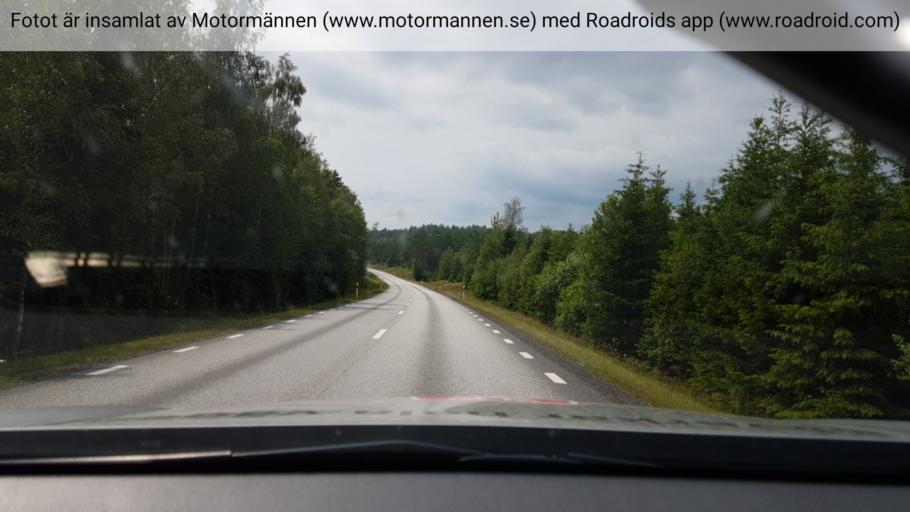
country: SE
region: Joenkoeping
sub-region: Mullsjo Kommun
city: Mullsjoe
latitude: 57.9284
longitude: 13.9178
